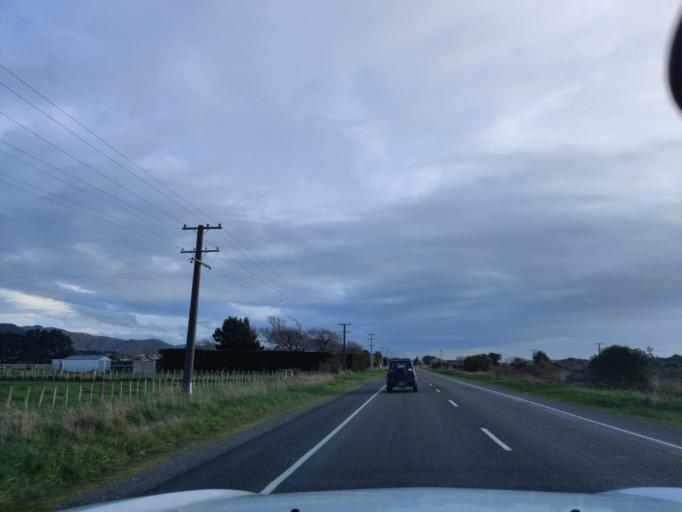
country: NZ
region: Manawatu-Wanganui
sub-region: Horowhenua District
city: Foxton
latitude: -40.5396
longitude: 175.4214
